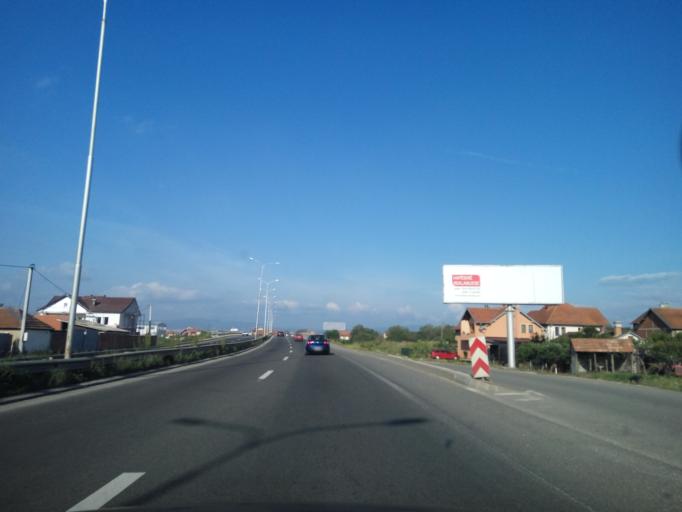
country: XK
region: Pristina
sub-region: Komuna e Gracanices
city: Glanica
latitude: 42.6087
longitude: 21.0592
